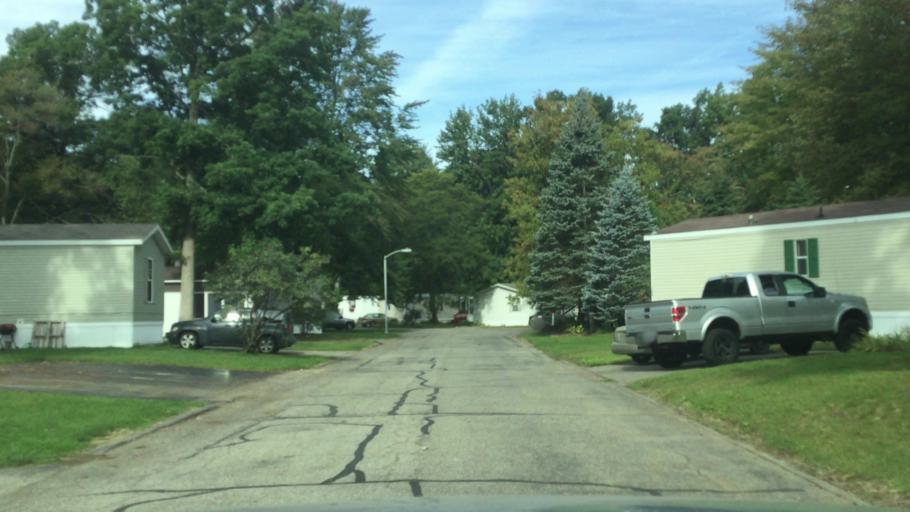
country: US
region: Michigan
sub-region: Oakland County
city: Holly
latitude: 42.8129
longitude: -83.6217
